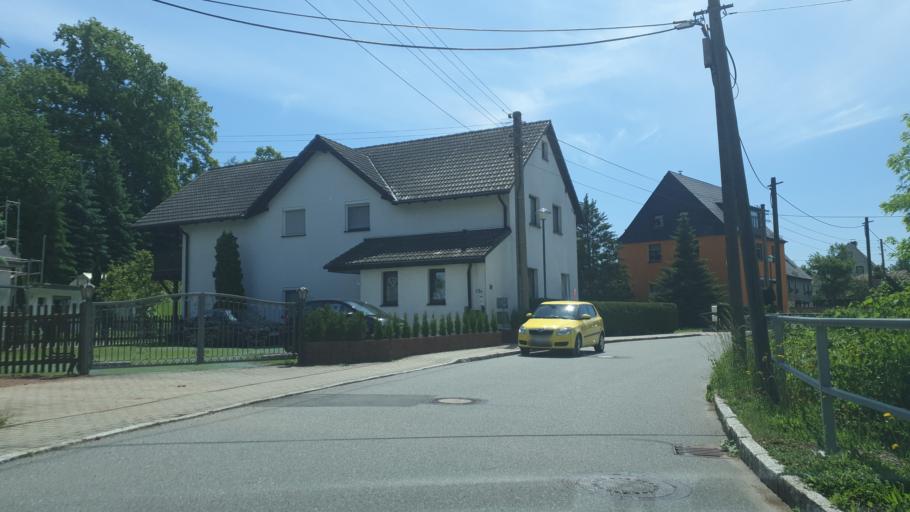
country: DE
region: Saxony
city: Niederdorf
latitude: 50.7269
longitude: 12.7898
